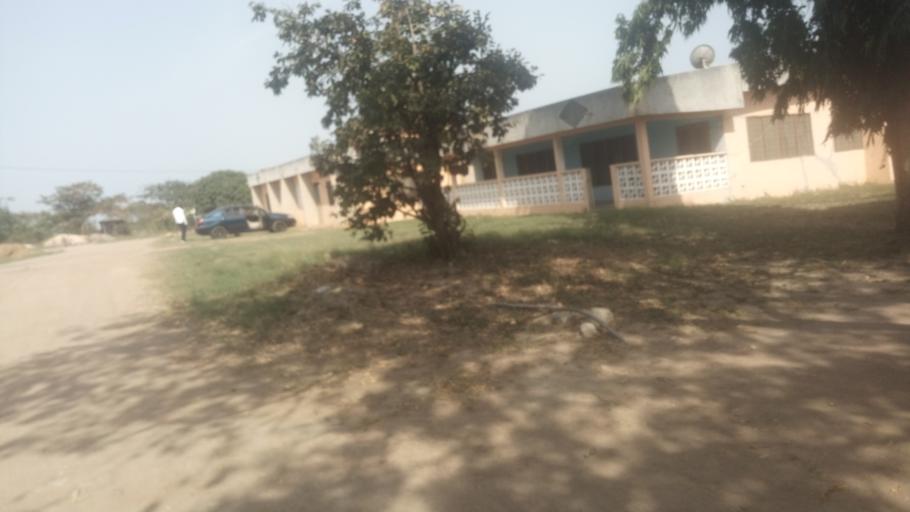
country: GH
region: Central
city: Winneba
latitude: 5.3798
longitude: -0.6448
